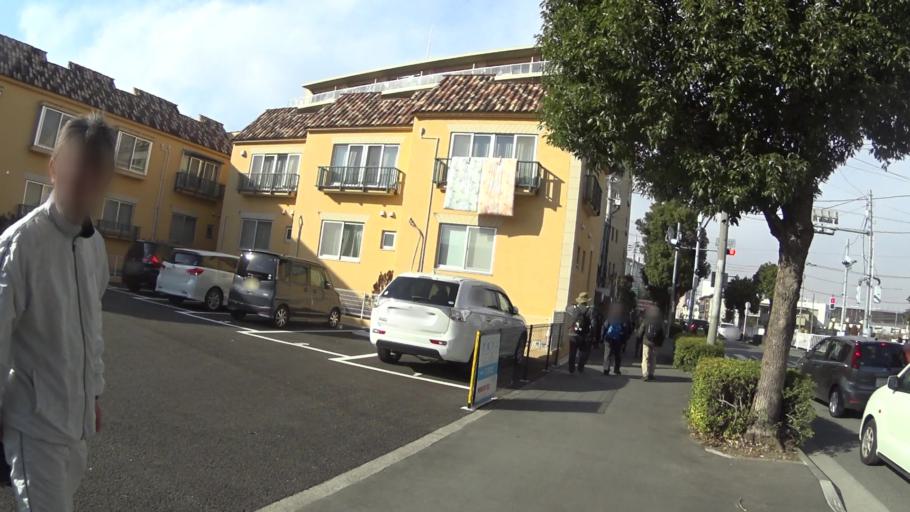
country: JP
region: Tokyo
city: Kokubunji
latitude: 35.6574
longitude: 139.4802
